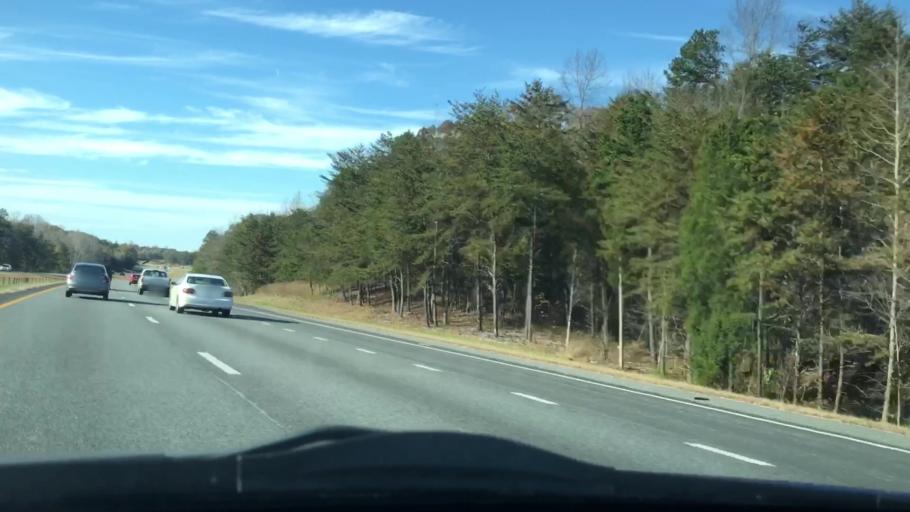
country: US
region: North Carolina
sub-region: Guilford County
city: High Point
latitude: 36.0196
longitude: -80.0477
